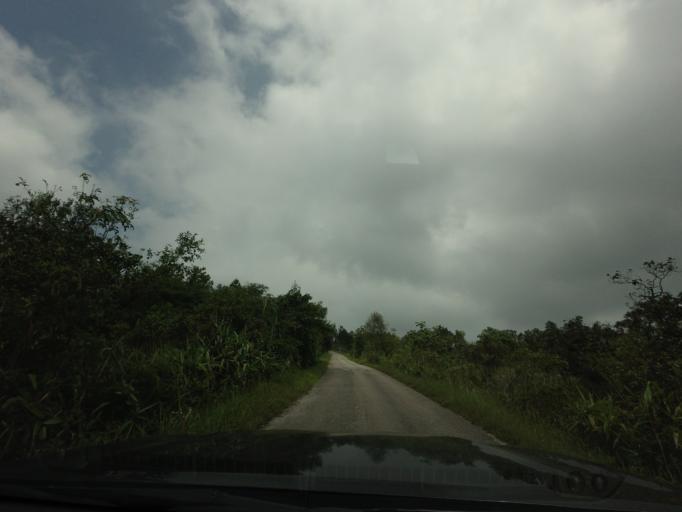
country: TH
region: Loei
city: Phu Ruea
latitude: 17.5032
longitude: 101.3482
